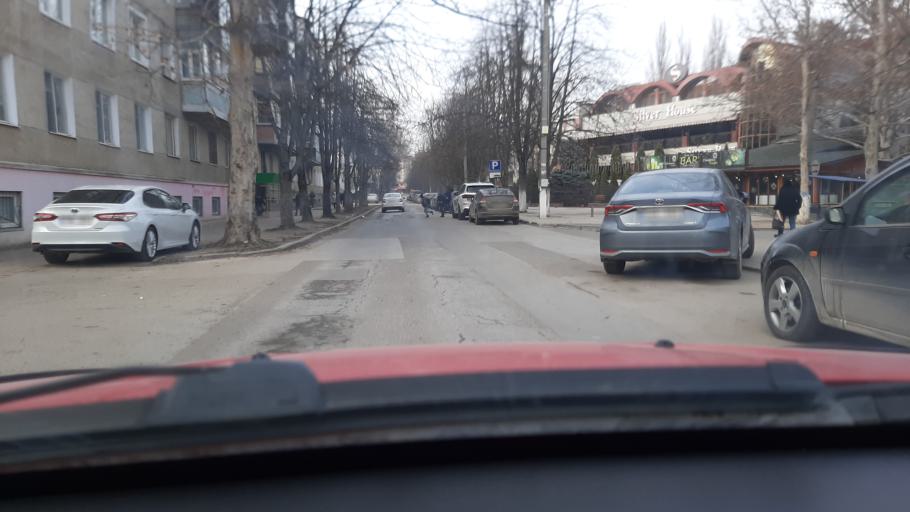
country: MD
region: Chisinau
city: Chisinau
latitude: 47.0300
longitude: 28.7939
